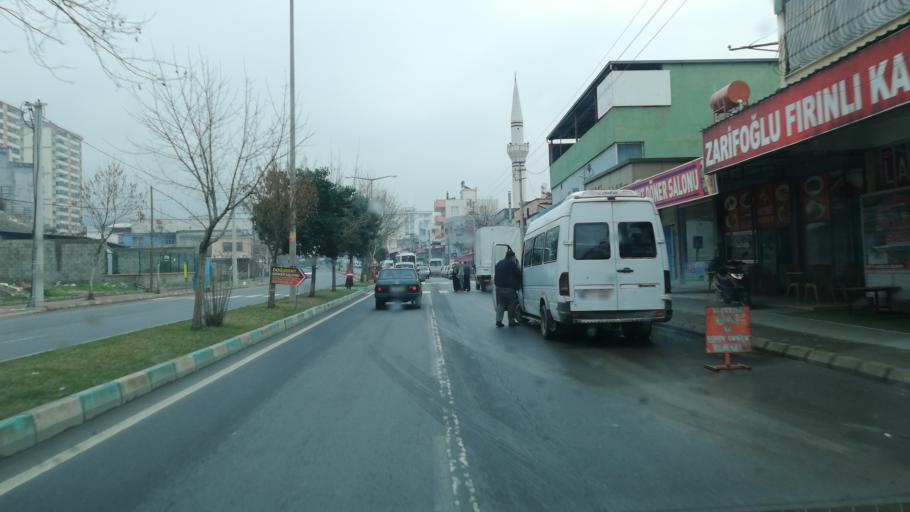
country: TR
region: Kahramanmaras
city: Kahramanmaras
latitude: 37.5816
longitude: 36.9611
